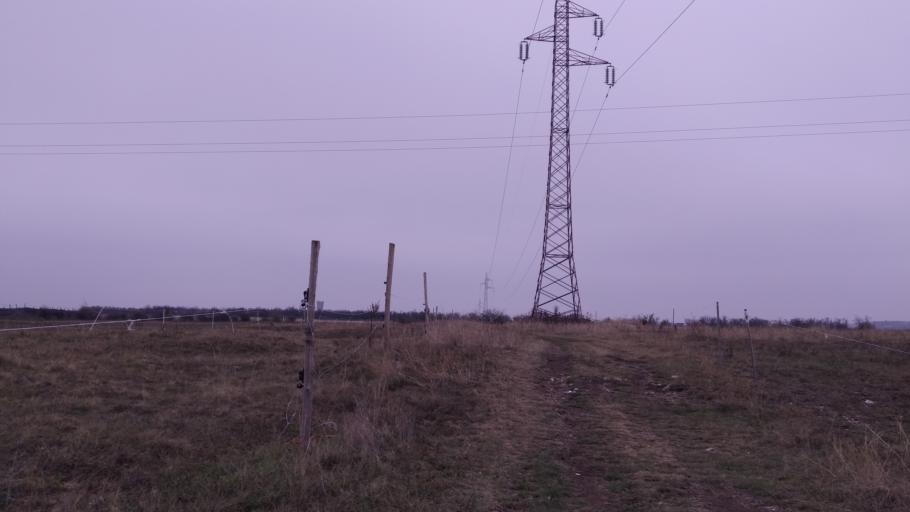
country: HU
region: Pest
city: Nagykovacsi
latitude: 47.6409
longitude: 19.0061
